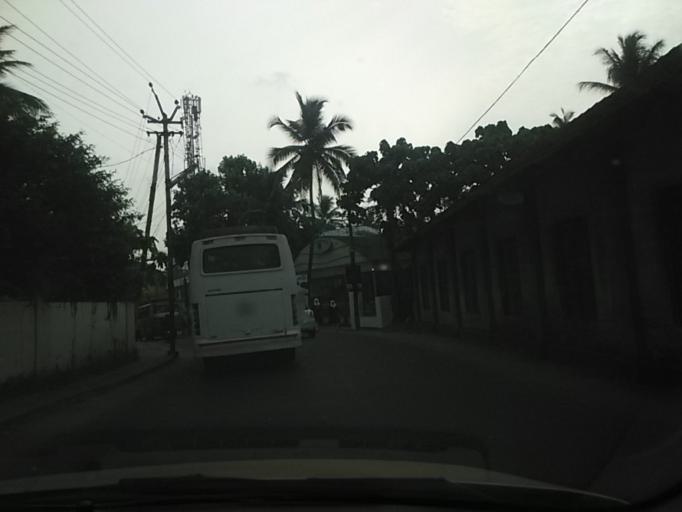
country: IN
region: Kerala
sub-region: Kozhikode
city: Kozhikode
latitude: 11.2718
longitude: 75.7759
